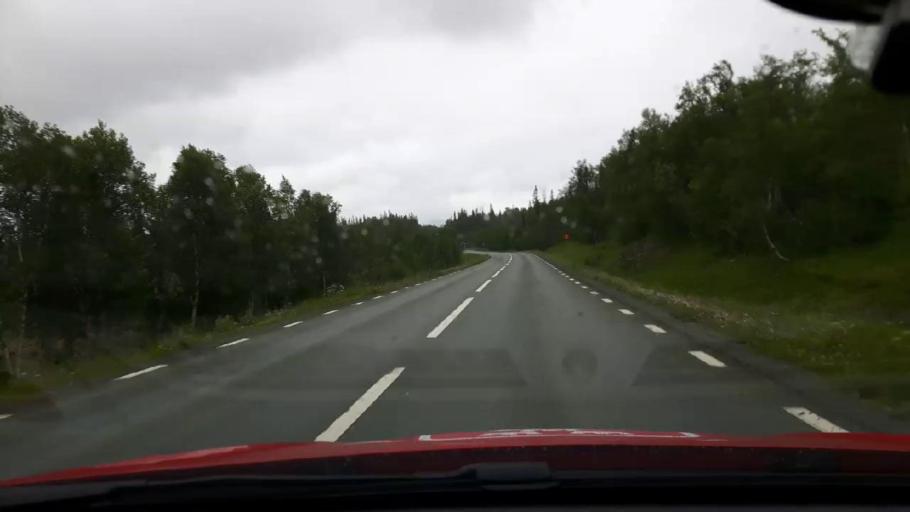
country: NO
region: Nord-Trondelag
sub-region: Meraker
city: Meraker
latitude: 63.3078
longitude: 12.1084
